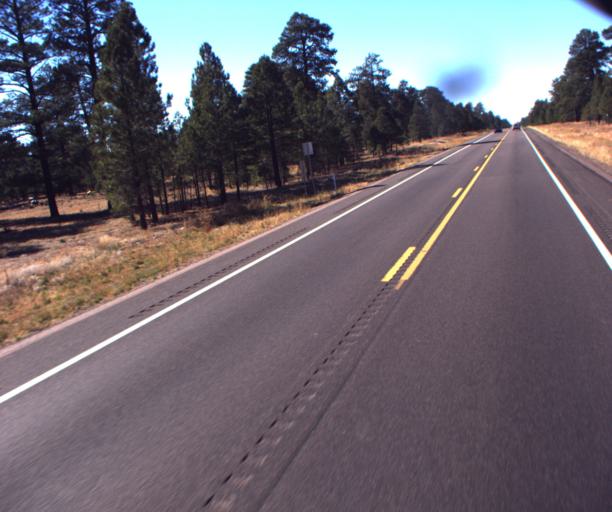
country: US
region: Arizona
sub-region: Apache County
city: Saint Michaels
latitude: 35.6878
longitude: -109.2466
